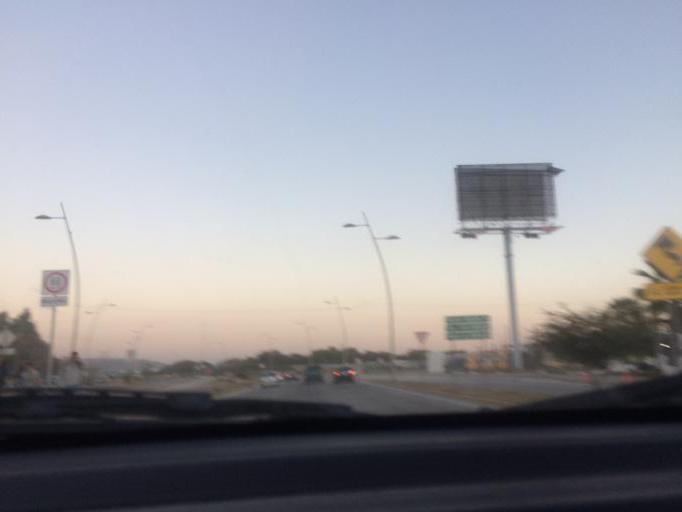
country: MX
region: Guanajuato
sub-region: Leon
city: Medina
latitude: 21.1396
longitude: -101.6296
